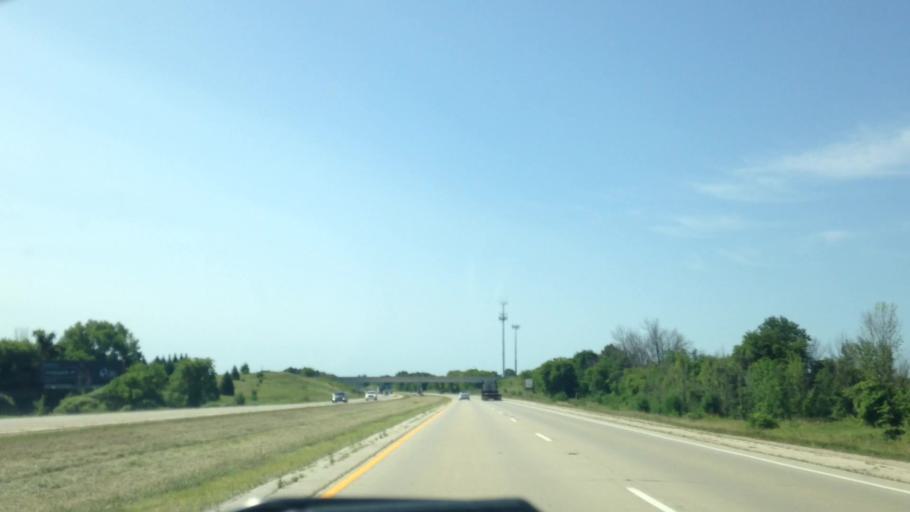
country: US
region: Wisconsin
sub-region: Washington County
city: Jackson
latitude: 43.3425
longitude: -88.1910
